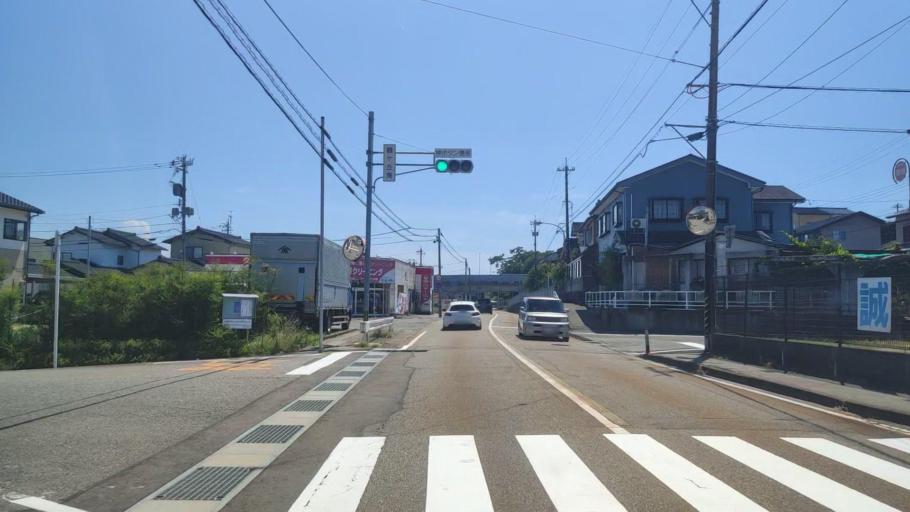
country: JP
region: Ishikawa
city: Kanazawa-shi
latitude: 36.6385
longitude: 136.6404
